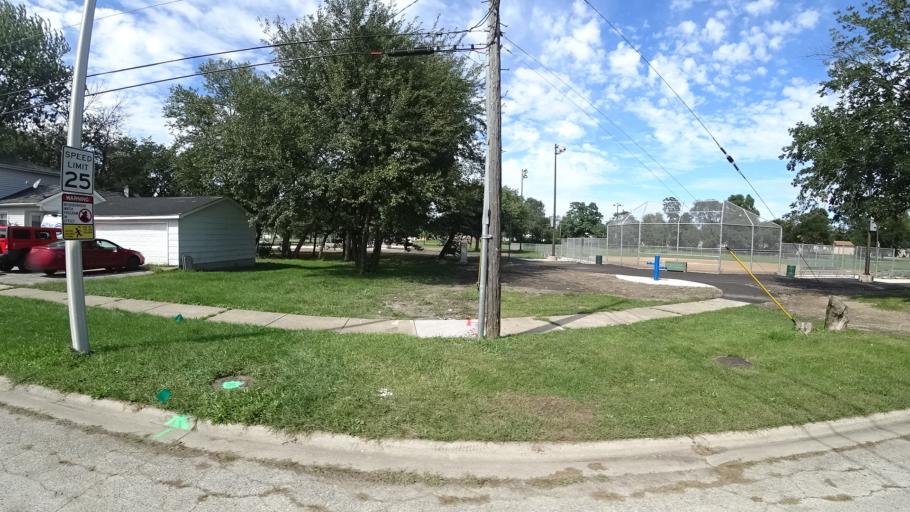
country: US
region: Illinois
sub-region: Cook County
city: Chicago Ridge
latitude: 41.7106
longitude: -87.7727
